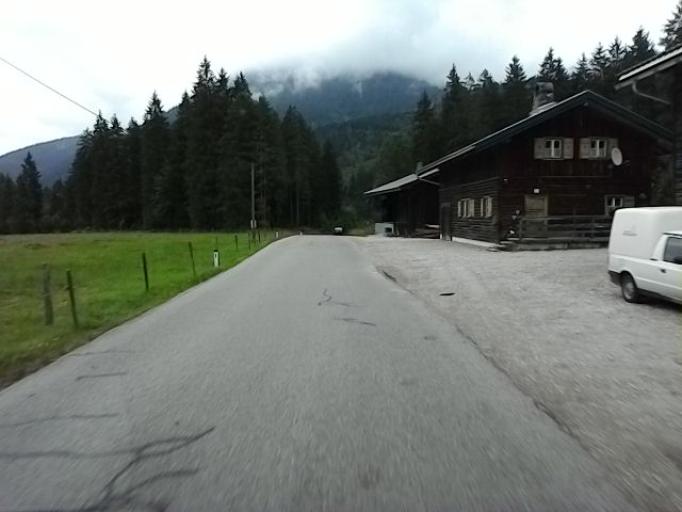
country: DE
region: Bavaria
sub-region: Upper Bavaria
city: Jachenau
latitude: 47.4798
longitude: 11.4629
